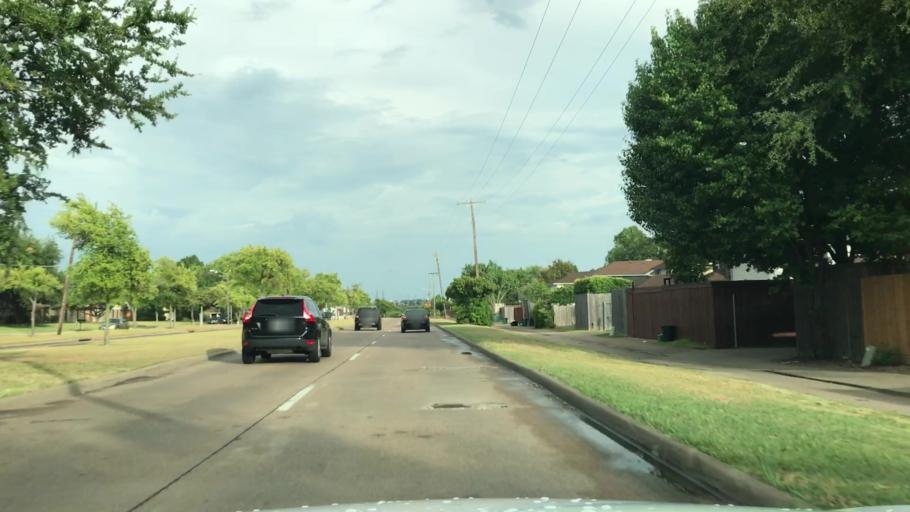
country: US
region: Texas
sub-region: Dallas County
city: Garland
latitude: 32.8442
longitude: -96.6279
